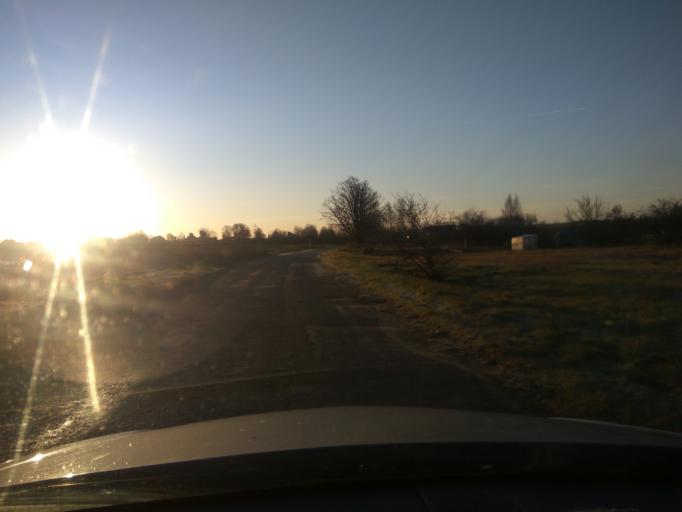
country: LV
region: Kuldigas Rajons
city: Kuldiga
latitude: 56.9646
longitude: 22.0048
